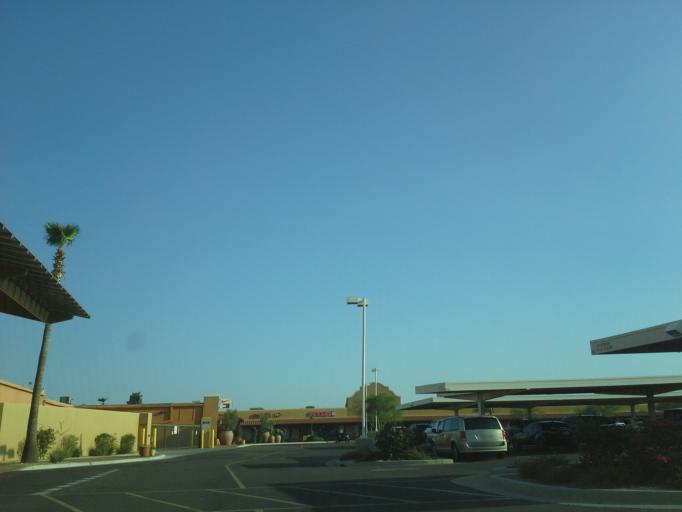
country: US
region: Arizona
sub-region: Maricopa County
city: Anthem
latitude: 33.8756
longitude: -112.1493
